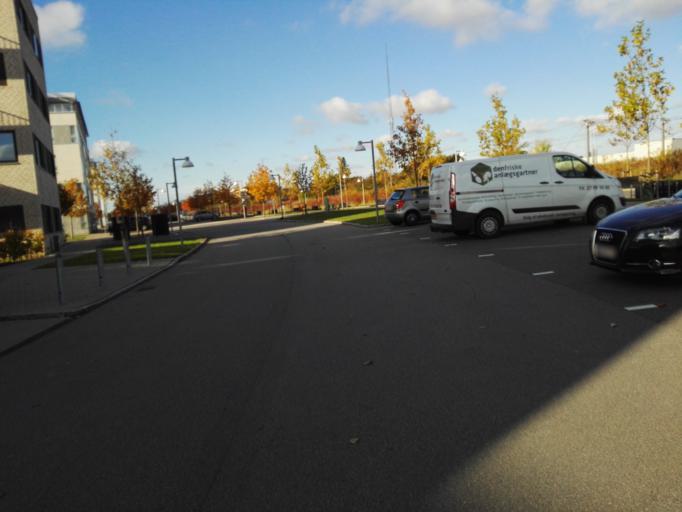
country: DK
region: Capital Region
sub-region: Ballerup Kommune
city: Malov
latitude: 55.7448
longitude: 12.3221
